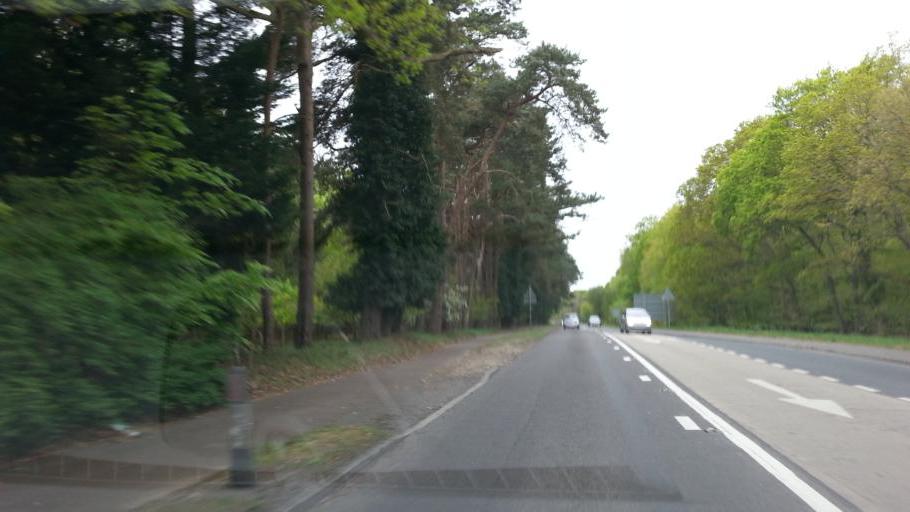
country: GB
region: England
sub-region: Suffolk
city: Lakenheath
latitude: 52.3387
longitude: 0.5323
